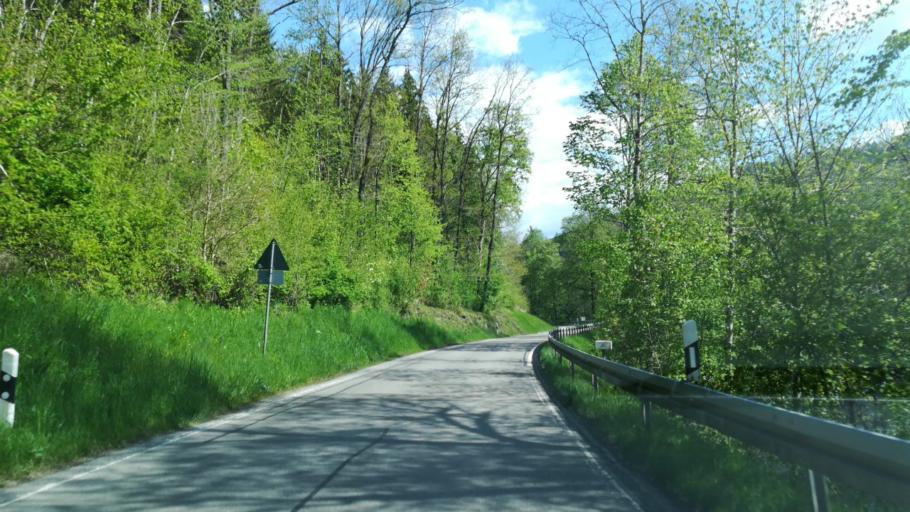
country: DE
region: Baden-Wuerttemberg
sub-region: Freiburg Region
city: Blumberg
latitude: 47.8424
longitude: 8.4770
